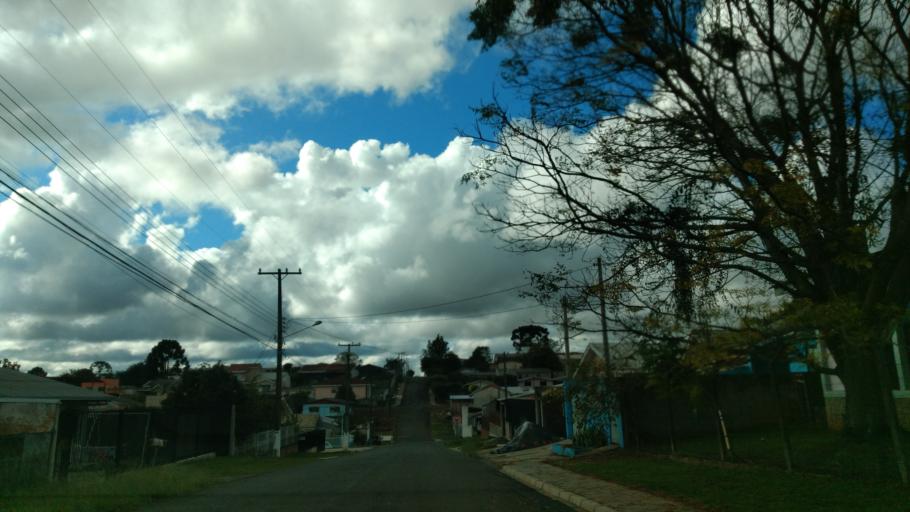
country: BR
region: Parana
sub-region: Guarapuava
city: Guarapuava
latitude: -25.3966
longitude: -51.4910
